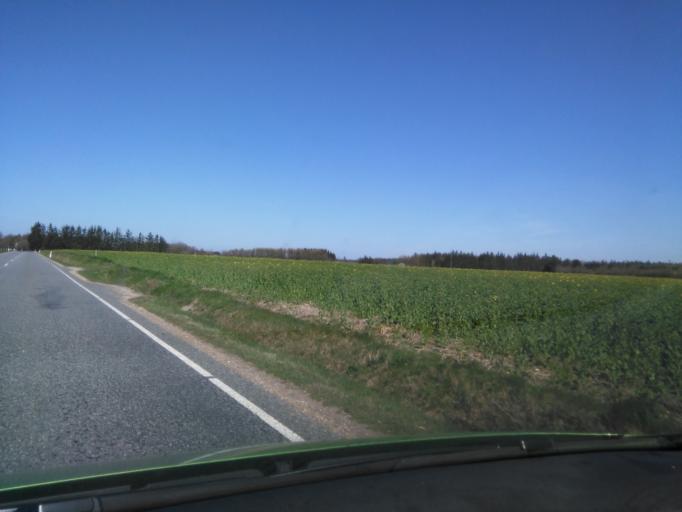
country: DK
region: South Denmark
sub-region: Varde Kommune
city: Olgod
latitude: 55.7164
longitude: 8.7379
